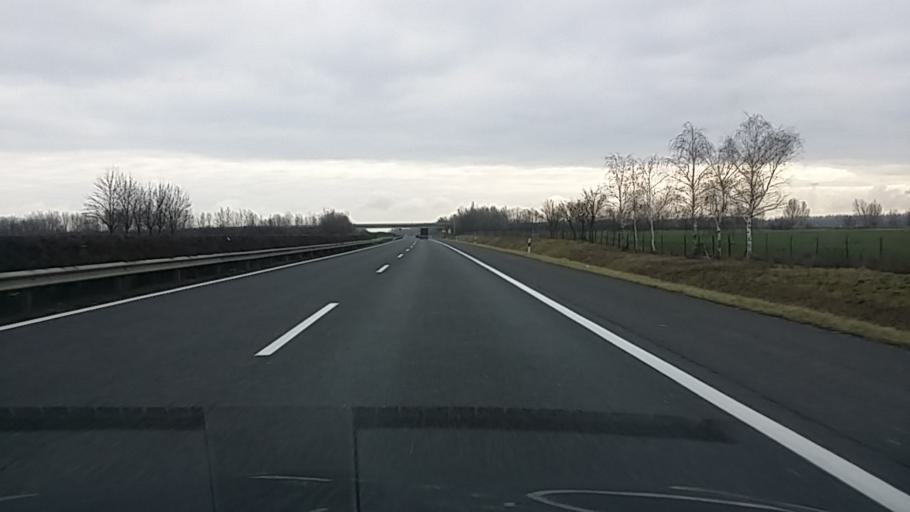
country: HU
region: Gyor-Moson-Sopron
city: Mosonszentmiklos
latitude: 47.7287
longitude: 17.4483
